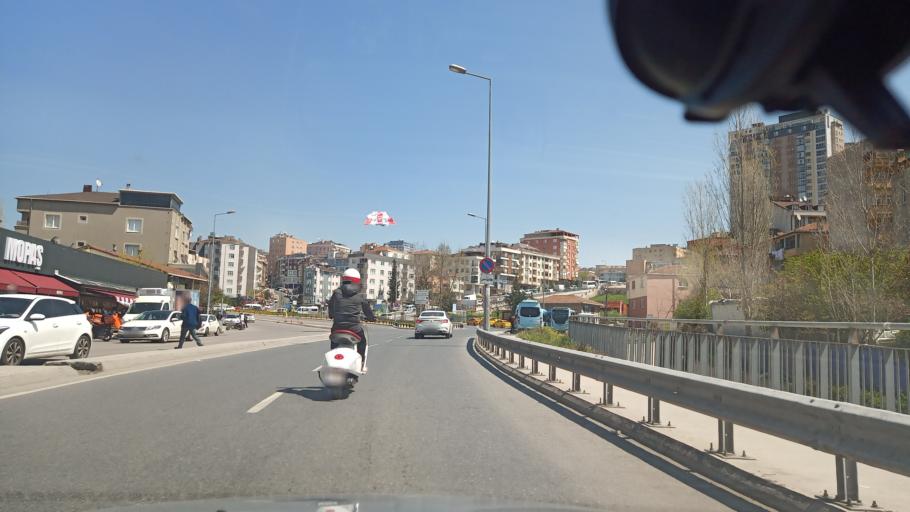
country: TR
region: Istanbul
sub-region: Atasehir
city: Atasehir
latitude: 40.9673
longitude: 29.1214
